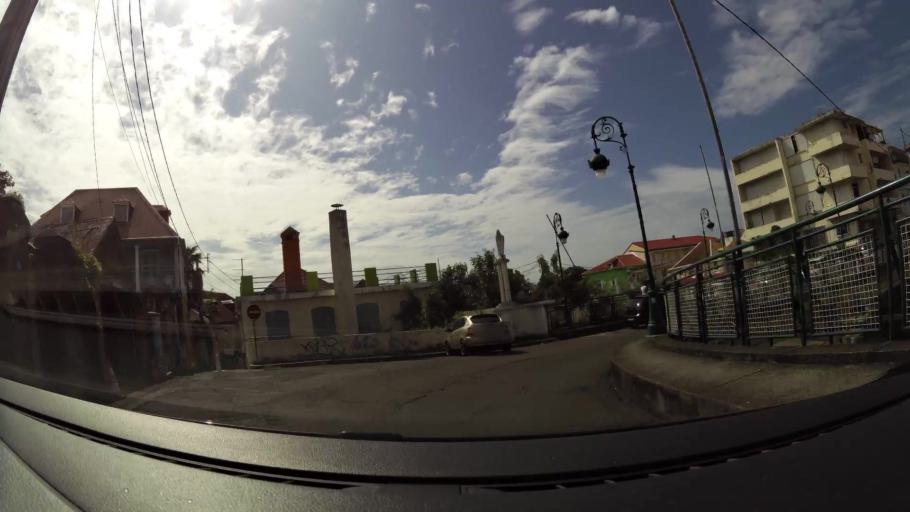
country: GP
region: Guadeloupe
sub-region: Guadeloupe
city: Basse-Terre
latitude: 15.9948
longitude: -61.7293
